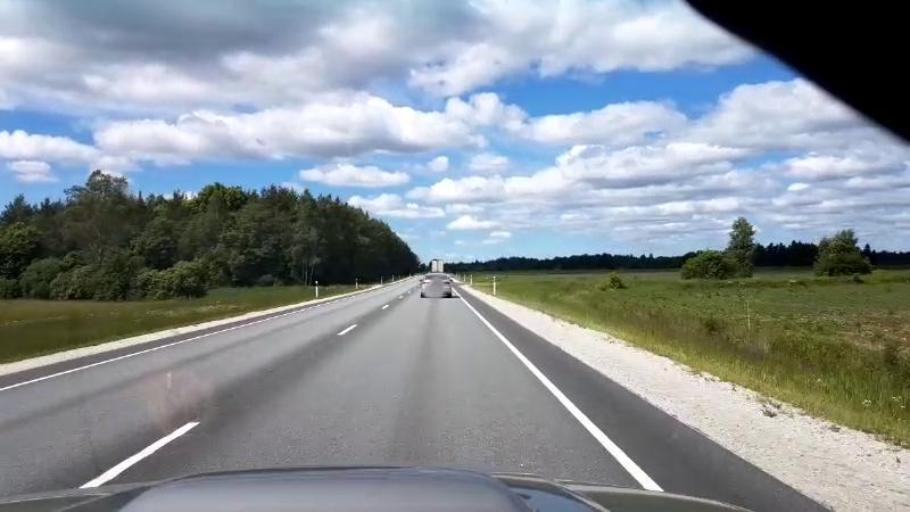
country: EE
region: Paernumaa
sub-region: Halinga vald
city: Parnu-Jaagupi
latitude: 58.6638
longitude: 24.4623
